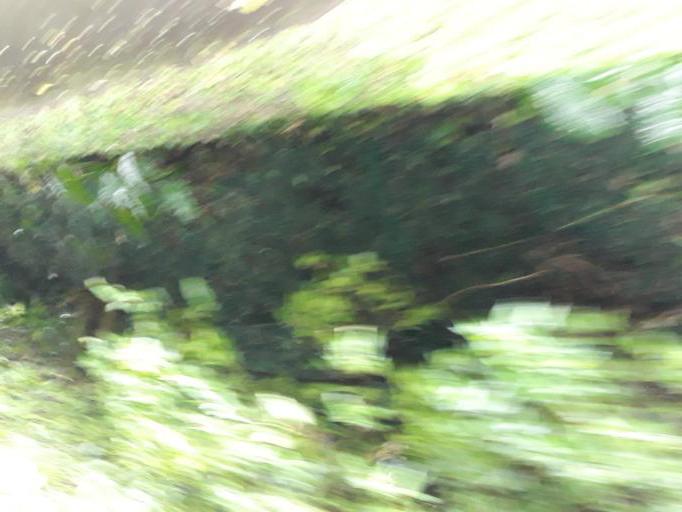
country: TW
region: Taipei
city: Taipei
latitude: 24.9903
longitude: 121.5887
